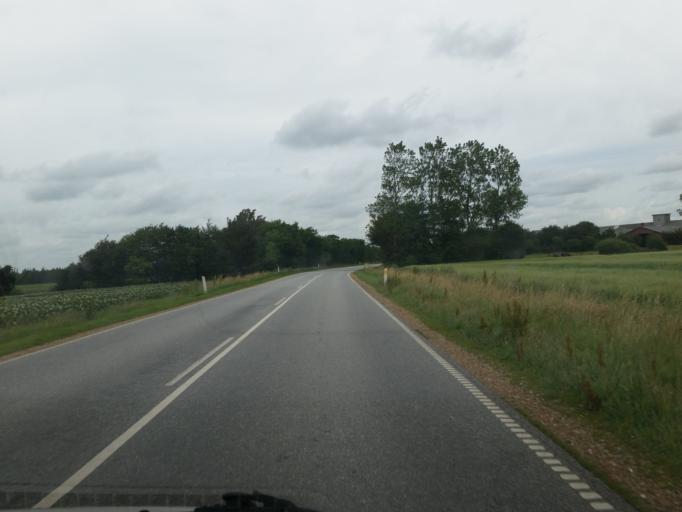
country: DK
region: South Denmark
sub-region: Esbjerg Kommune
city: Ribe
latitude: 55.3701
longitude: 8.8096
